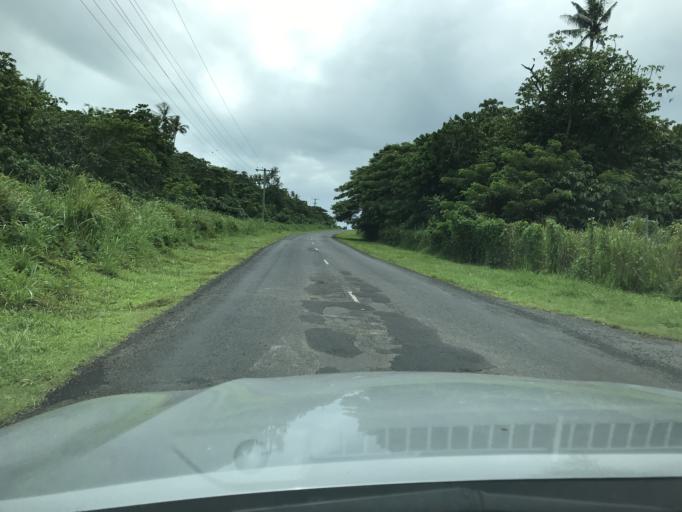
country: WS
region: Aiga-i-le-Tai
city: Mulifanua
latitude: -13.8340
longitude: -172.0151
